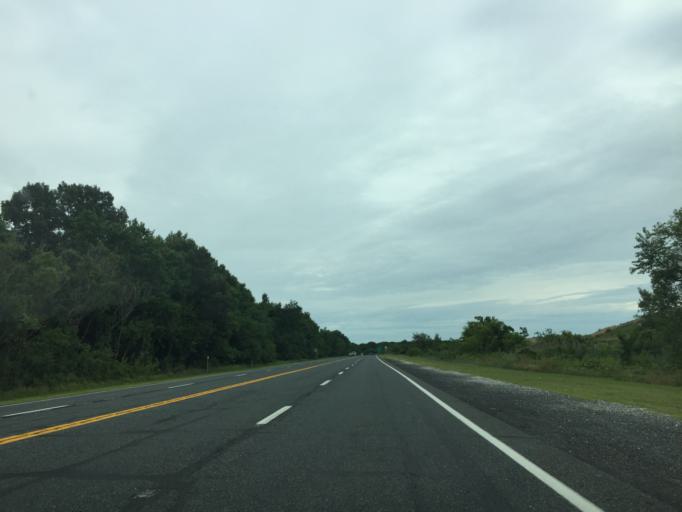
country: US
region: Maryland
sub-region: Baltimore County
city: Dundalk
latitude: 39.2459
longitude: -76.4859
